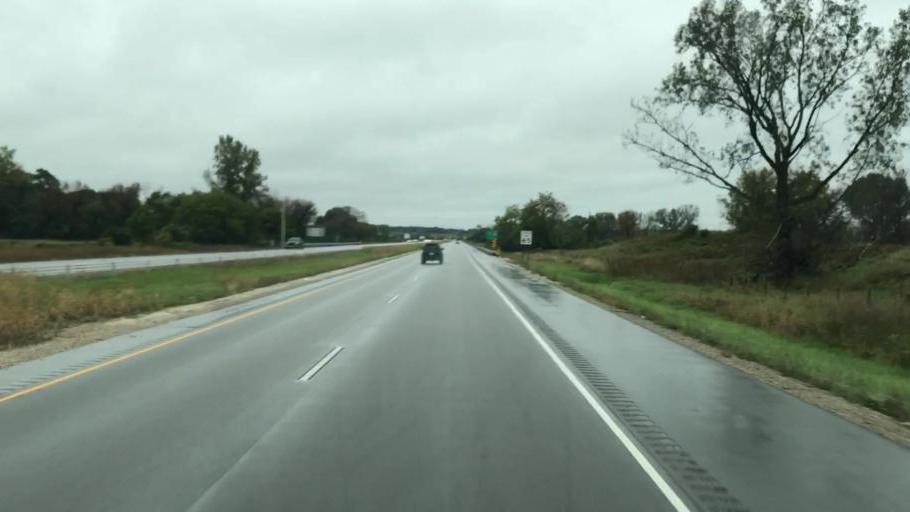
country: US
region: Wisconsin
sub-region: Waukesha County
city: Pewaukee
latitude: 43.0612
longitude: -88.2514
